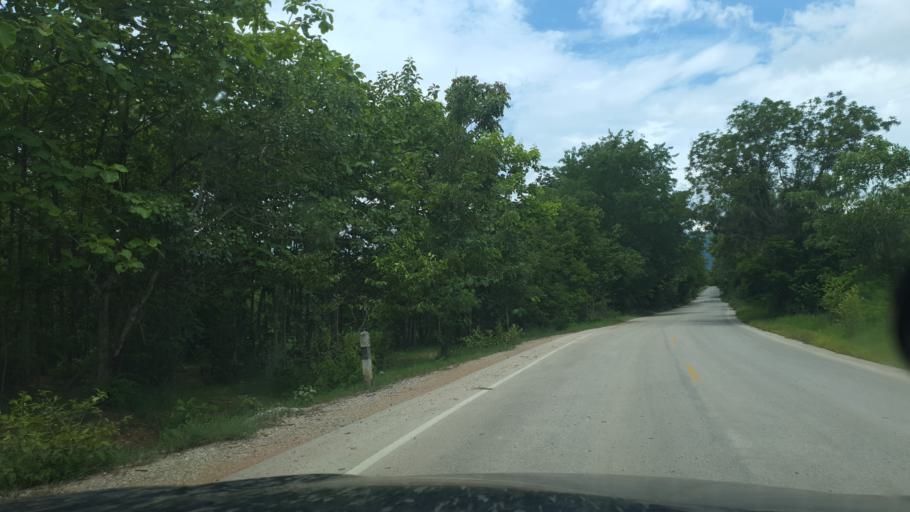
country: TH
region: Lampang
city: Sop Prap
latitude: 17.9264
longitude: 99.3783
